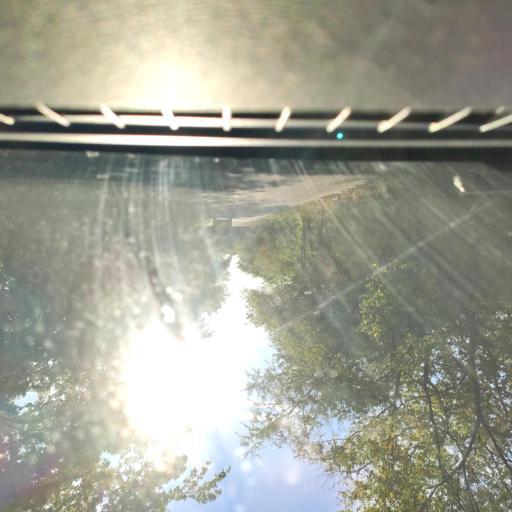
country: RU
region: Voronezj
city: Novaya Usman'
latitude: 51.6393
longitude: 39.3044
